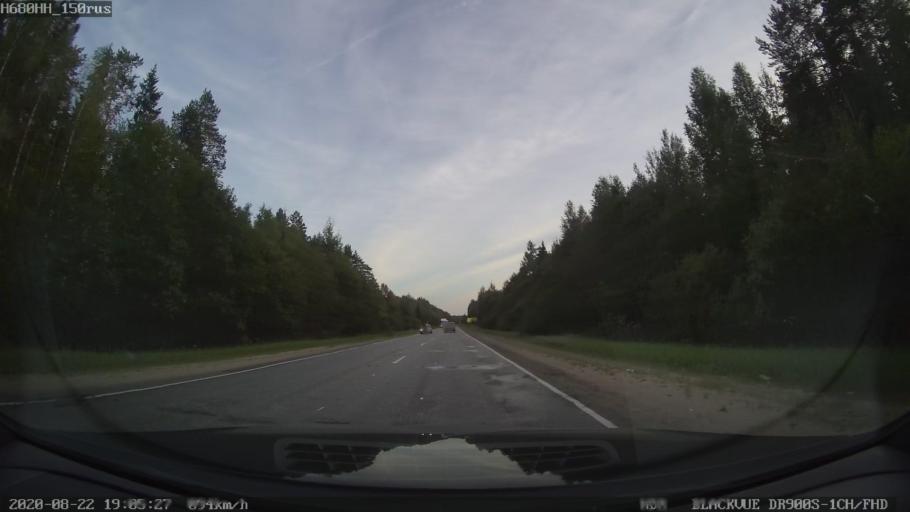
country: RU
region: Tverskaya
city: Sakharovo
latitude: 57.0764
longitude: 36.1118
